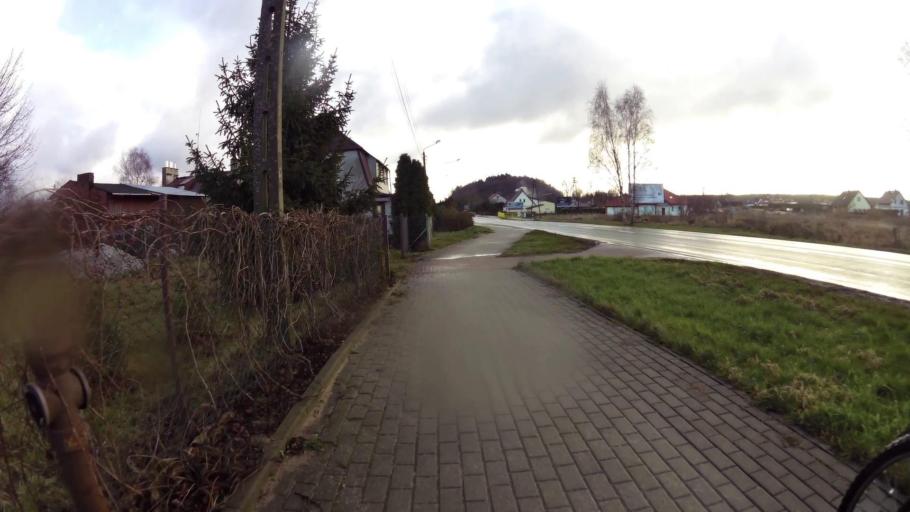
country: PL
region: West Pomeranian Voivodeship
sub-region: Powiat koszalinski
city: Sianow
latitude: 54.1314
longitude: 16.2901
